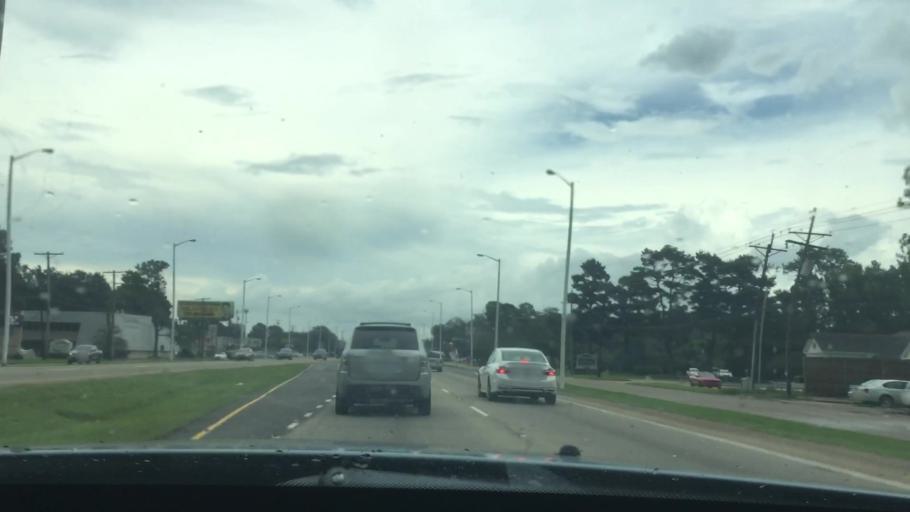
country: US
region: Louisiana
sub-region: East Baton Rouge Parish
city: Monticello
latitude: 30.4575
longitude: -91.0664
